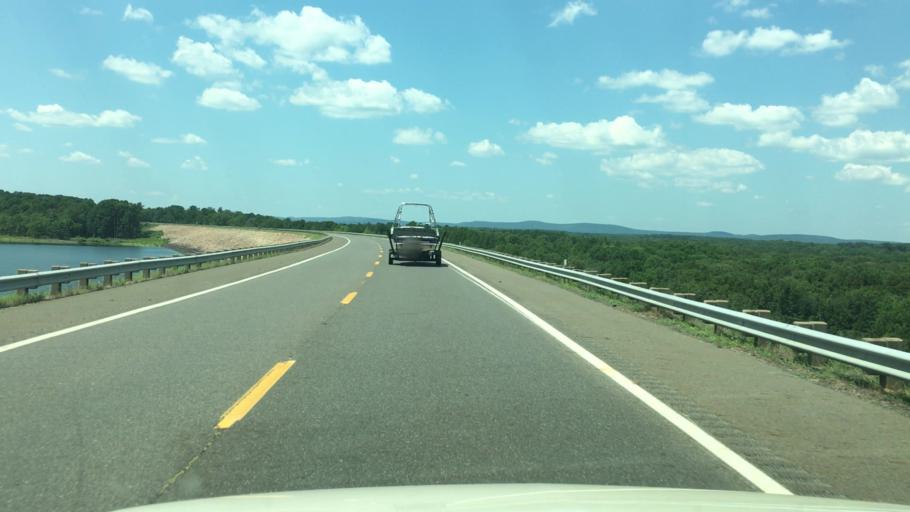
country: US
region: Arkansas
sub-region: Clark County
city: Arkadelphia
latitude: 34.2405
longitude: -93.1041
